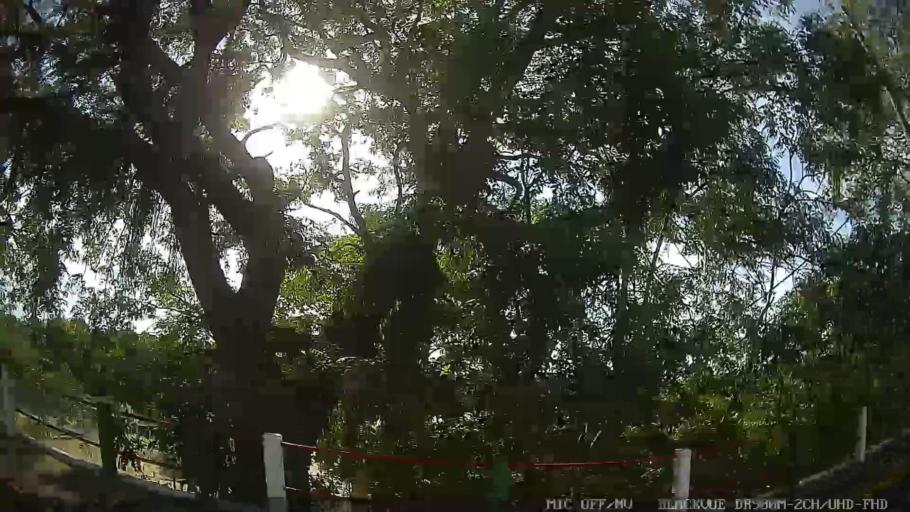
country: BR
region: Sao Paulo
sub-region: Laranjal Paulista
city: Laranjal Paulista
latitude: -23.0817
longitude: -47.7914
